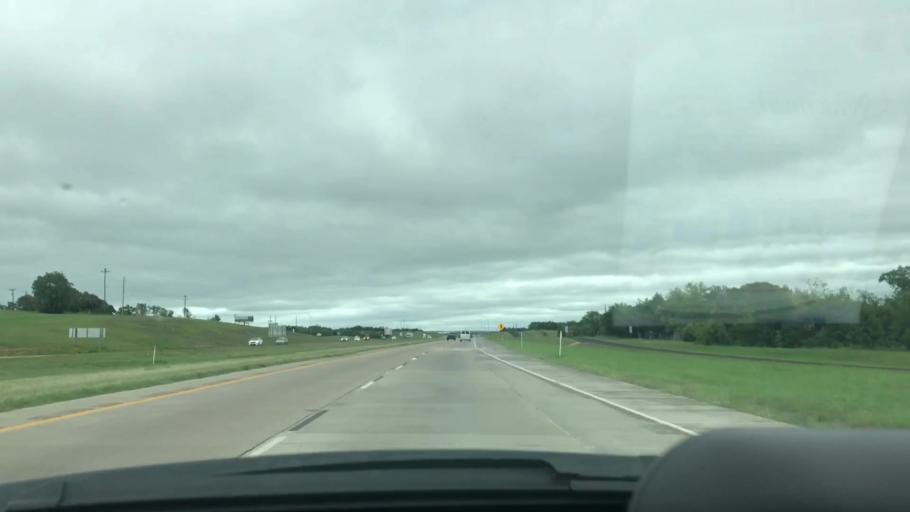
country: US
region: Texas
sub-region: Grayson County
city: Sherman
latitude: 33.6823
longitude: -96.6069
